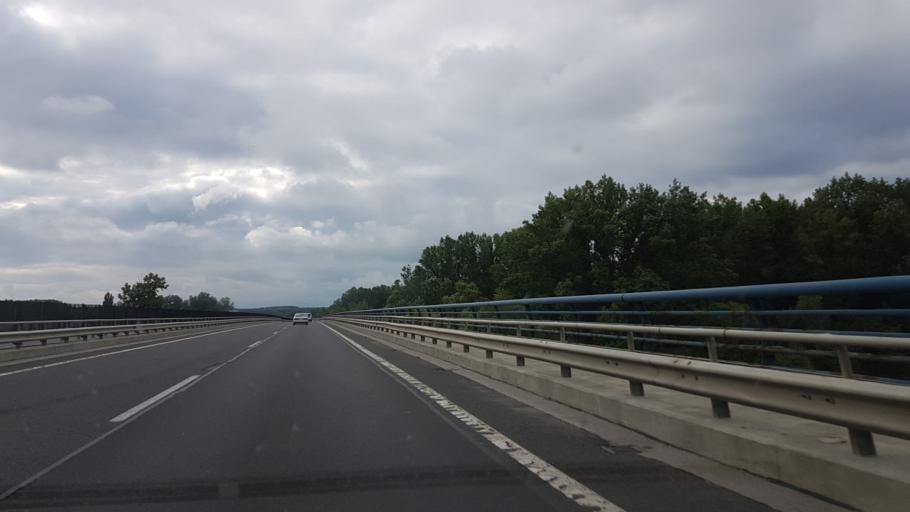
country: HU
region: Hajdu-Bihar
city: Polgar
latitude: 47.8557
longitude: 21.0544
